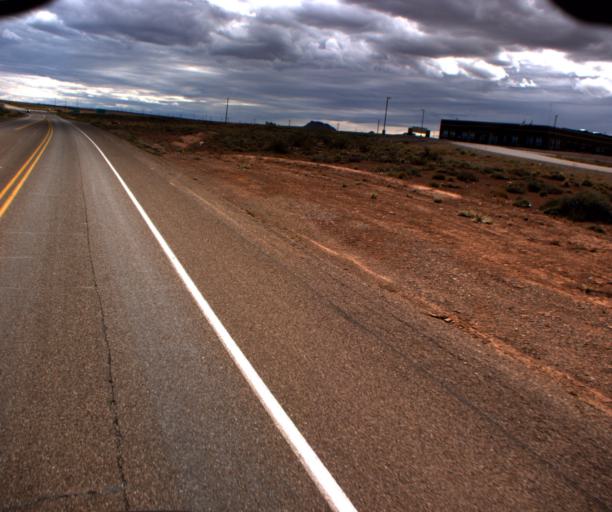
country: US
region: Arizona
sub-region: Navajo County
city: Holbrook
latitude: 34.8722
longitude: -110.1615
